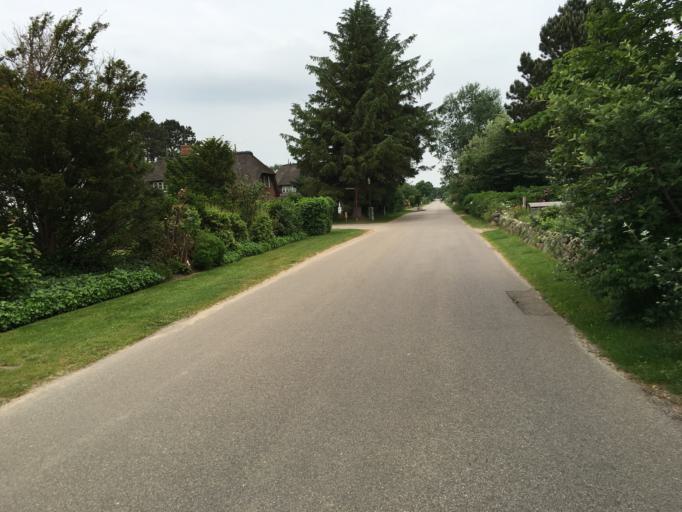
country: DE
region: Schleswig-Holstein
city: Norddorf
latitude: 54.6741
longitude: 8.3348
